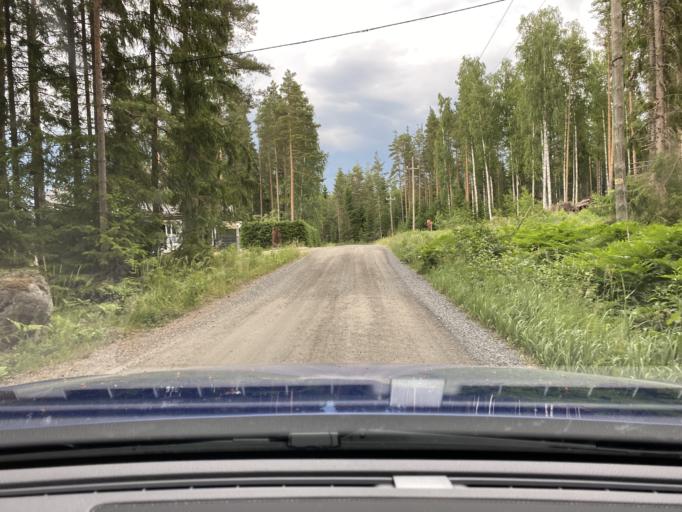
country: FI
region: Satakunta
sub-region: Rauma
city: Lappi
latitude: 61.1380
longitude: 21.9059
